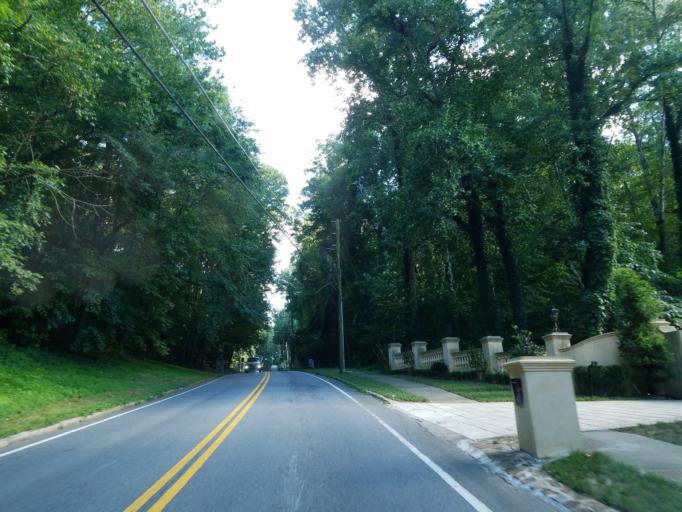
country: US
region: Georgia
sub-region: Fulton County
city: Sandy Springs
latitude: 33.9309
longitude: -84.4117
